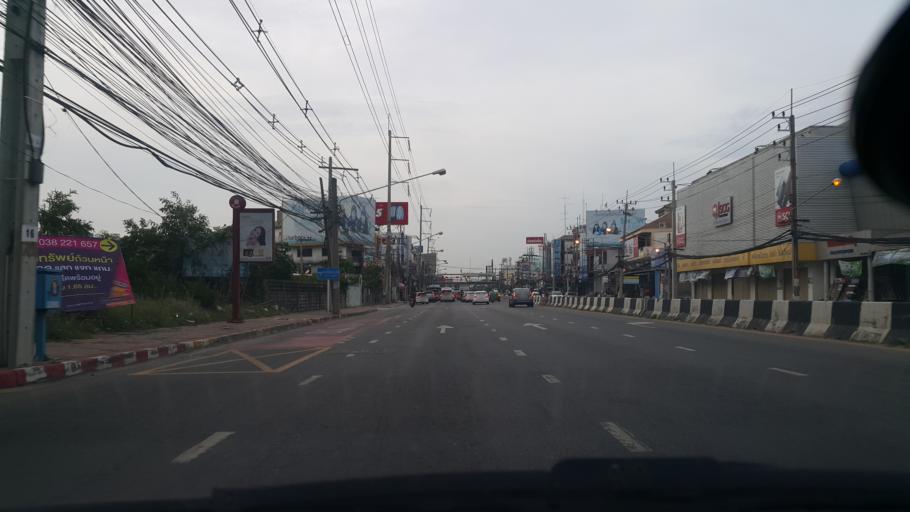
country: TH
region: Chon Buri
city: Phatthaya
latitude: 12.9653
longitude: 100.9098
